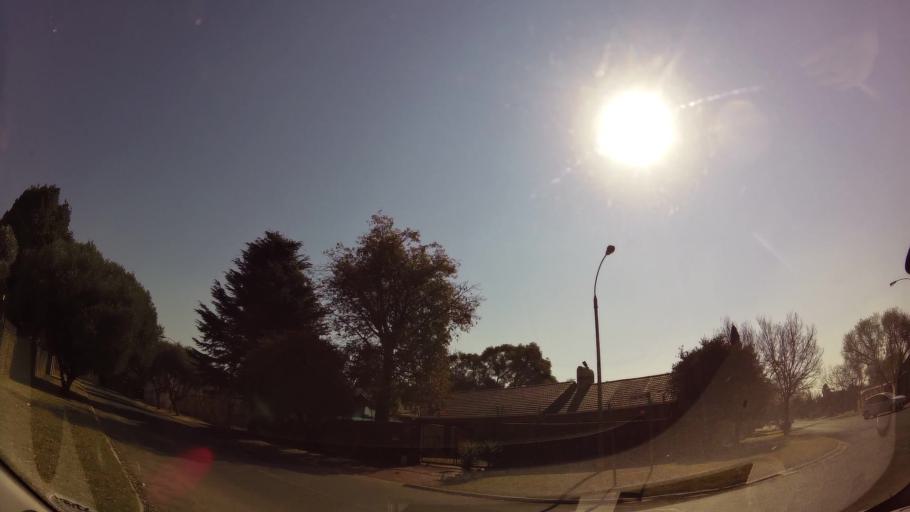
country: ZA
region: Gauteng
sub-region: Ekurhuleni Metropolitan Municipality
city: Boksburg
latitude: -26.1620
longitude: 28.2579
